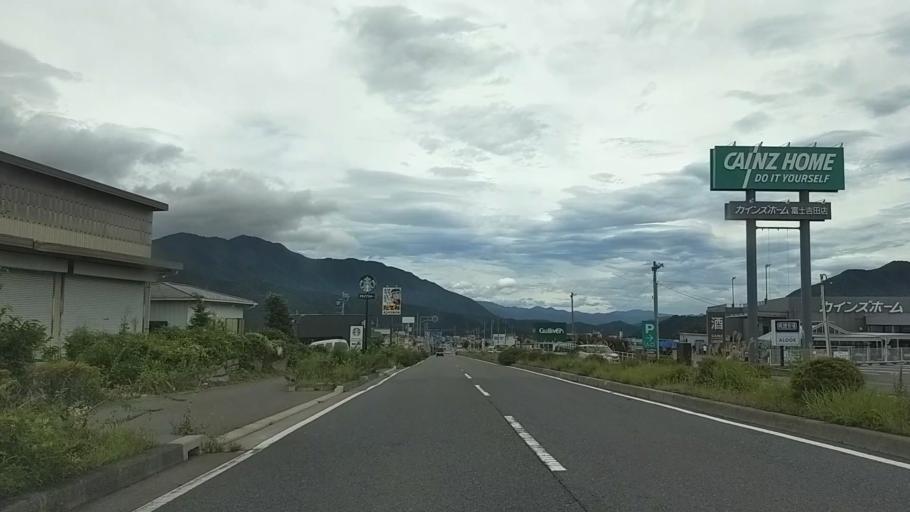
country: JP
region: Yamanashi
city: Fujikawaguchiko
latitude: 35.4745
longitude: 138.8077
